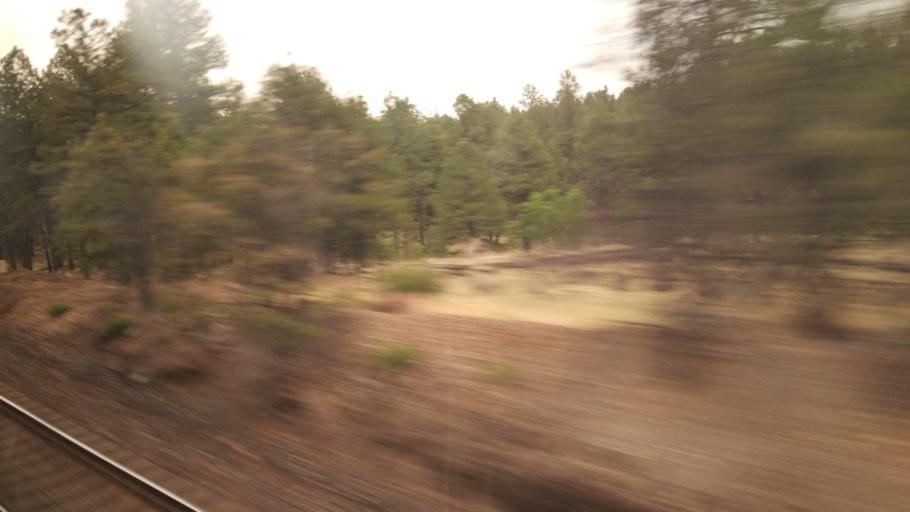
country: US
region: Arizona
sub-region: Coconino County
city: Parks
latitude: 35.2336
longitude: -112.0092
